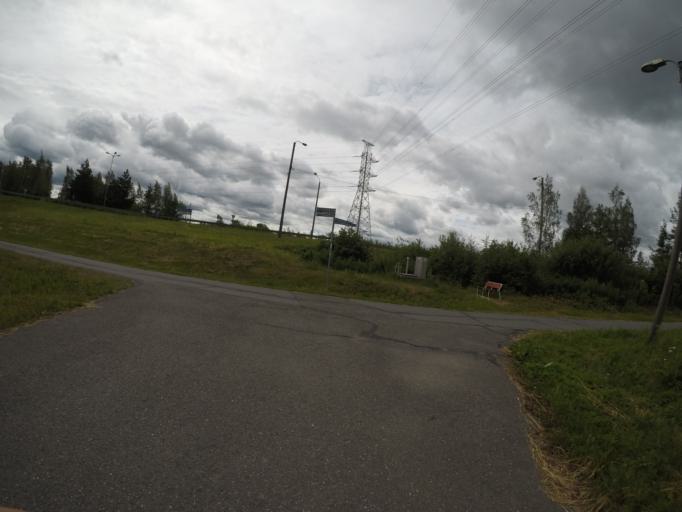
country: FI
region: Haeme
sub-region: Haemeenlinna
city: Haemeenlinna
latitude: 60.9966
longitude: 24.4936
